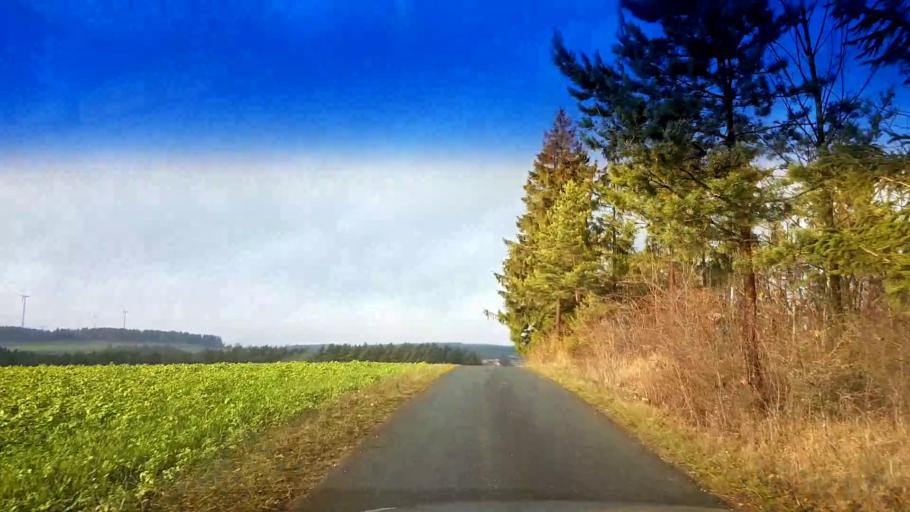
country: DE
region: Bavaria
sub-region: Upper Franconia
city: Poxdorf
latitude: 49.9242
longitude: 11.1261
